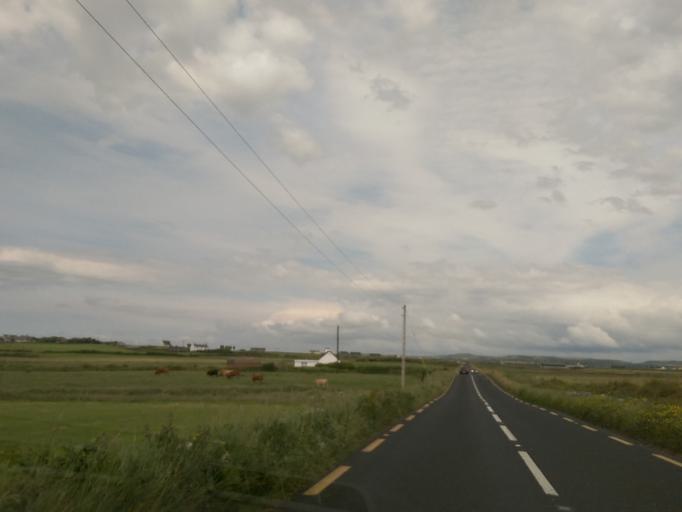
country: IE
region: Munster
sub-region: An Clar
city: Kilrush
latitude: 52.8239
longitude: -9.4457
